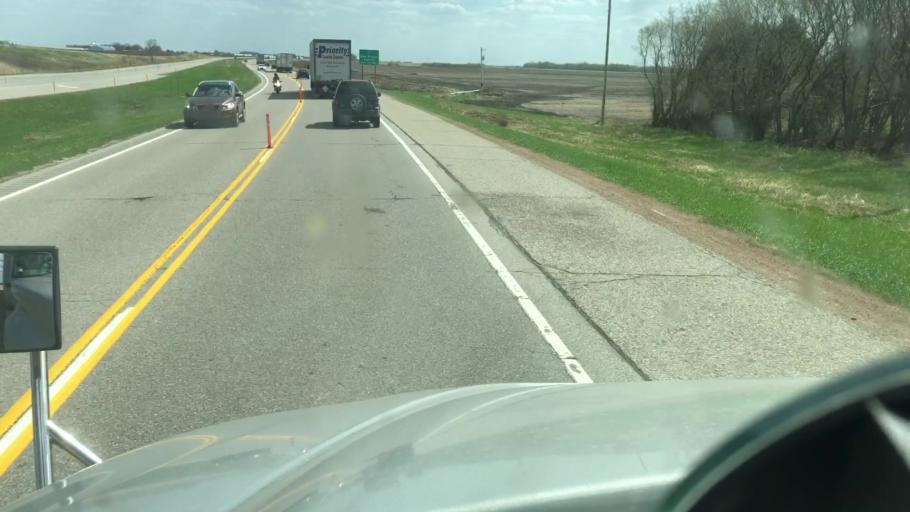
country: US
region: Minnesota
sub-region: Scott County
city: Belle Plaine
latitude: 44.5572
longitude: -93.8512
